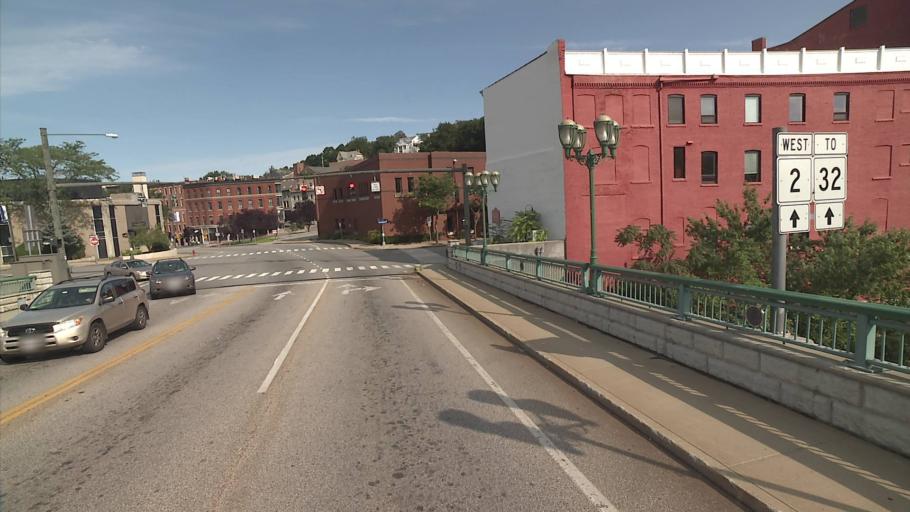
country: US
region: Connecticut
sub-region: New London County
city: Norwich
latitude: 41.5235
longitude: -72.0761
